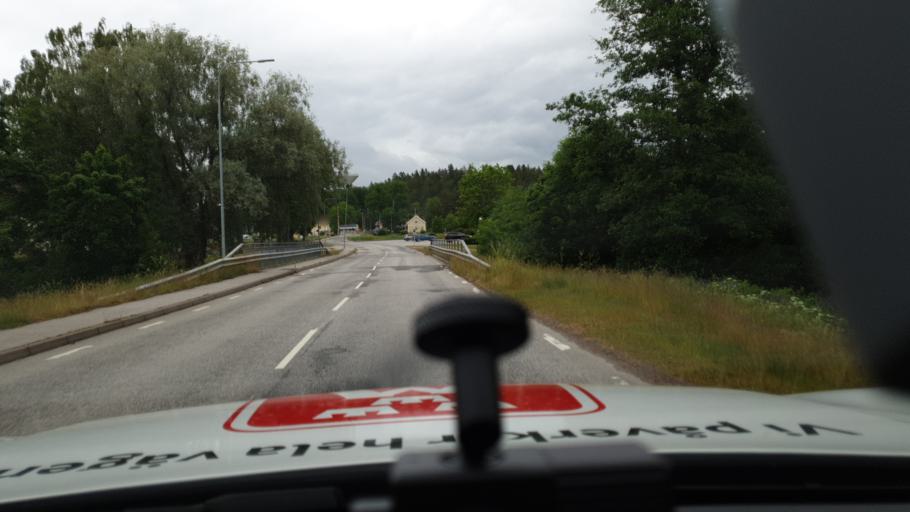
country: SE
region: Vaestra Goetaland
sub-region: Toreboda Kommun
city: Toereboda
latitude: 58.7997
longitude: 14.0558
